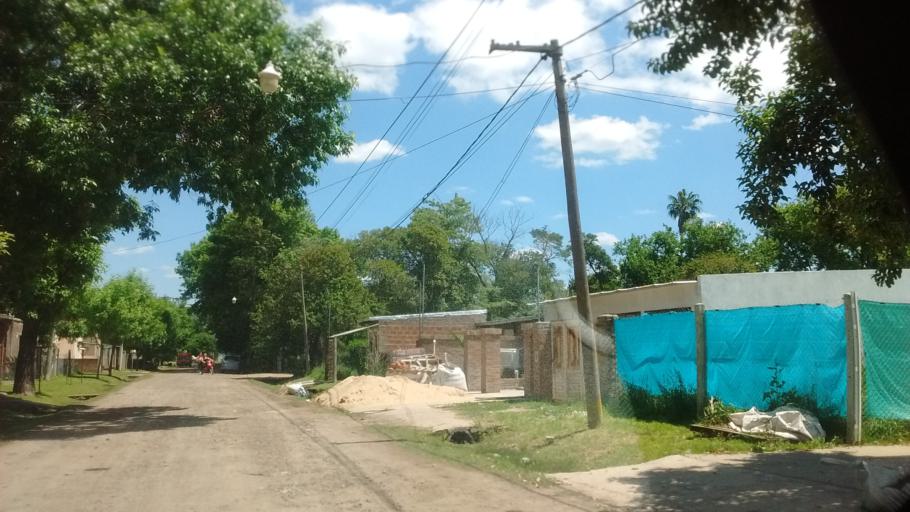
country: AR
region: Santa Fe
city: Funes
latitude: -32.8505
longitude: -60.7964
